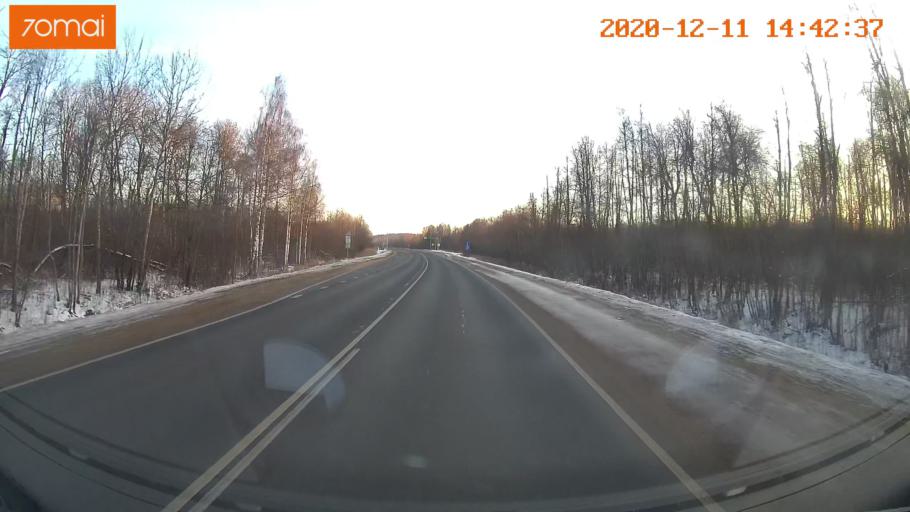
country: RU
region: Kostroma
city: Volgorechensk
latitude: 57.4827
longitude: 41.0619
